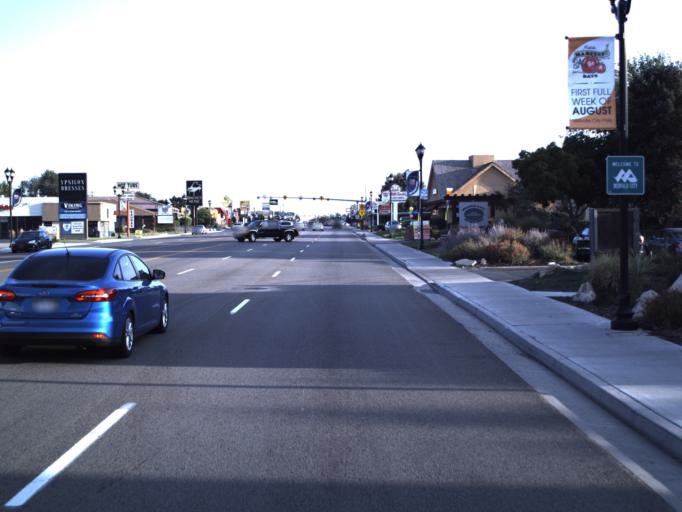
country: US
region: Utah
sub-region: Salt Lake County
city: Midvale
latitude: 40.6266
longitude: -111.8902
